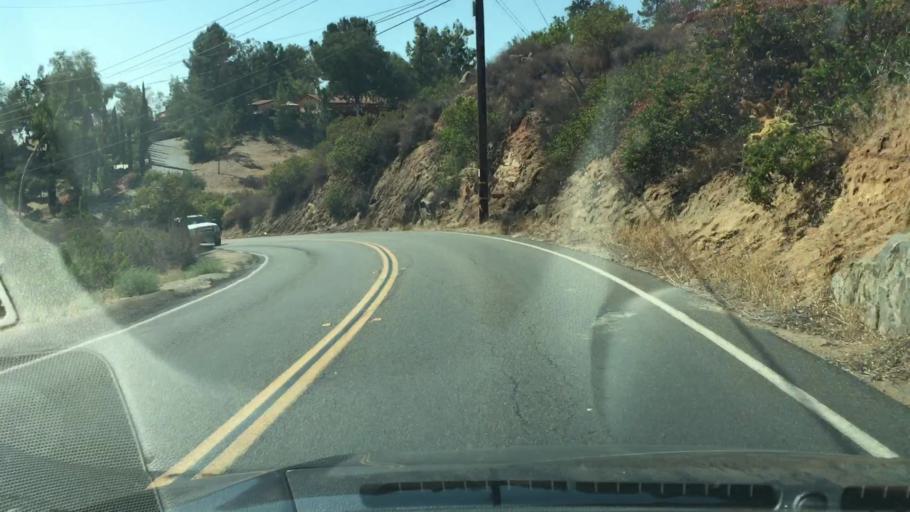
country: US
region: California
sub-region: San Diego County
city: Jamul
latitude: 32.7302
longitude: -116.8737
